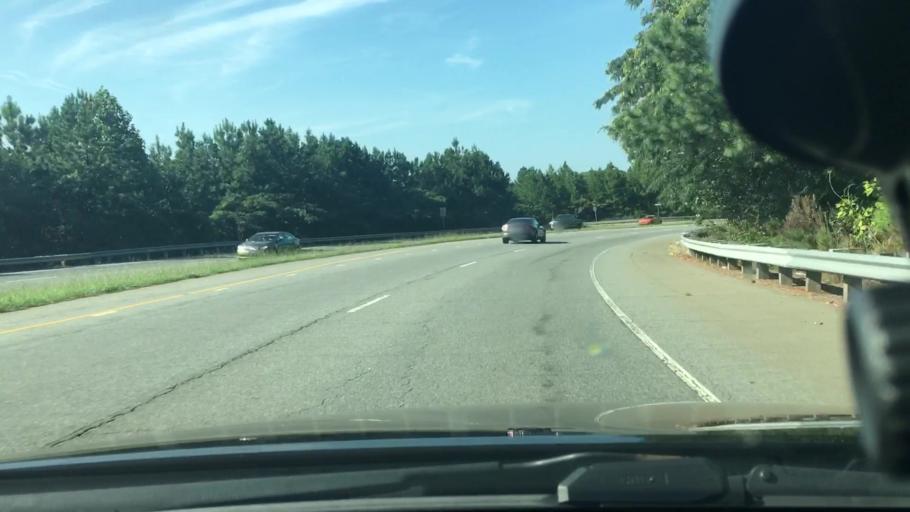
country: US
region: North Carolina
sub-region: Mecklenburg County
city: Mint Hill
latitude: 35.2102
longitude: -80.6630
